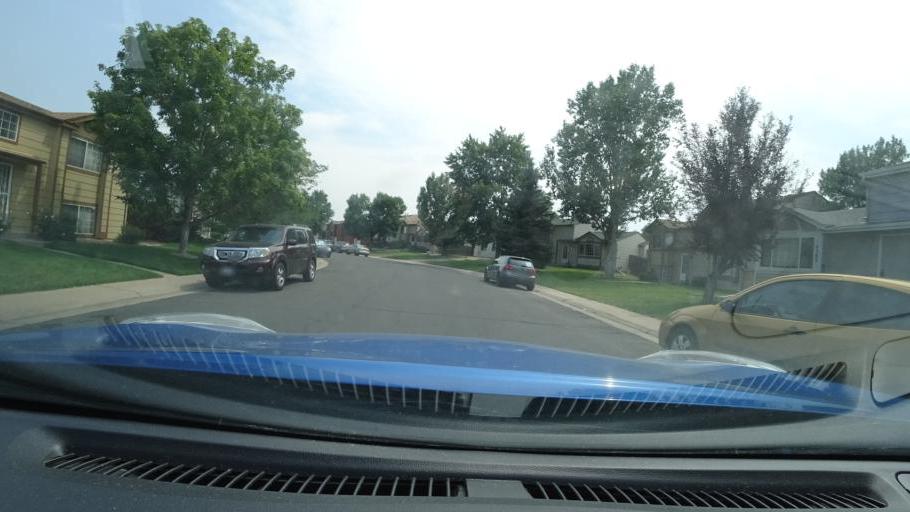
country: US
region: Colorado
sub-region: Adams County
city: Aurora
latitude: 39.7773
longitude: -104.7401
